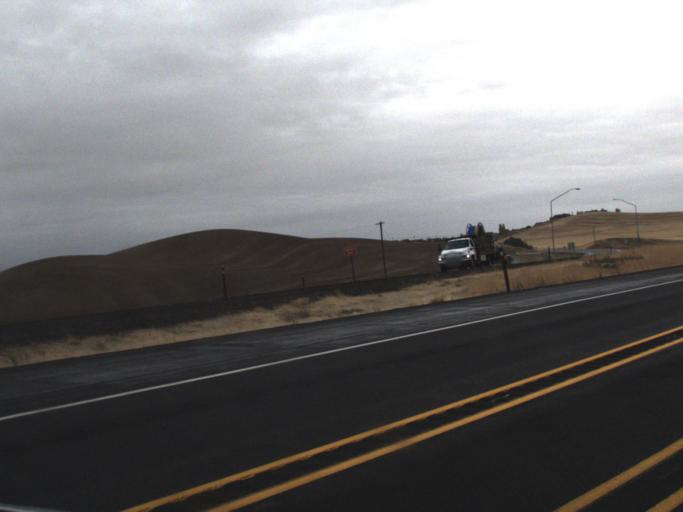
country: US
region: Washington
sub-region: Whitman County
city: Pullman
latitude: 46.7375
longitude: -117.2267
